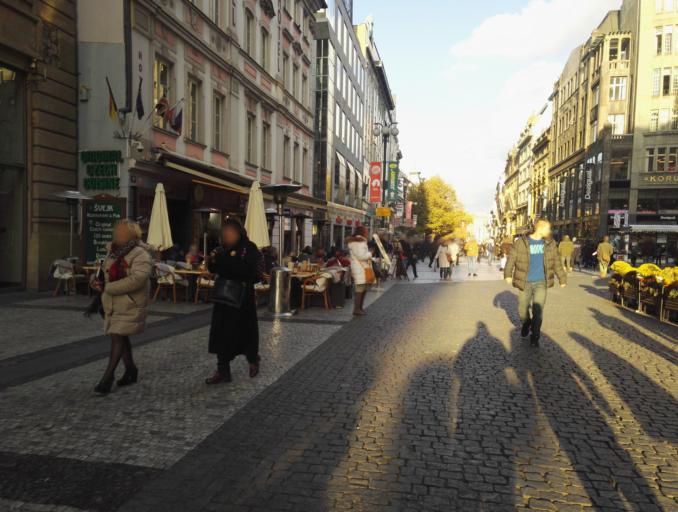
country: CZ
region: Praha
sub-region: Praha 1
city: Stare Mesto
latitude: 50.0840
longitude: 14.4230
